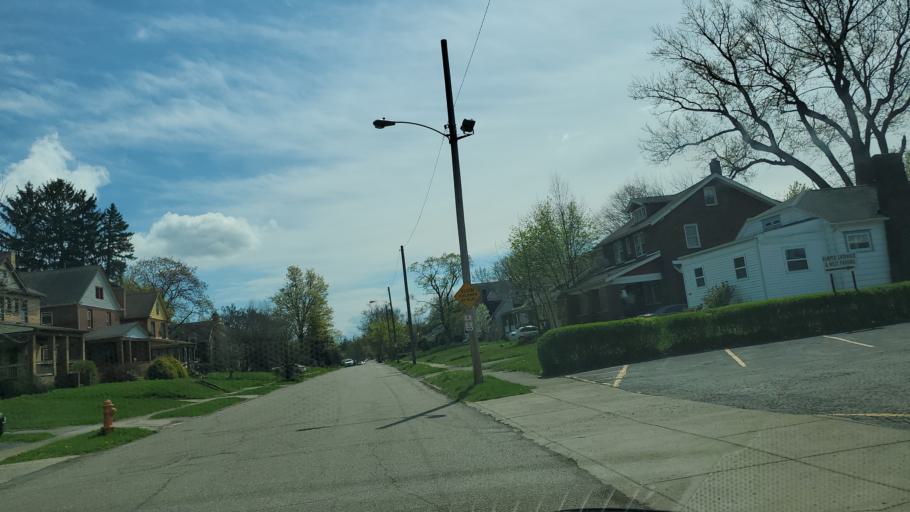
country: US
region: Ohio
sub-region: Mahoning County
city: Boardman
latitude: 41.0605
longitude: -80.6591
